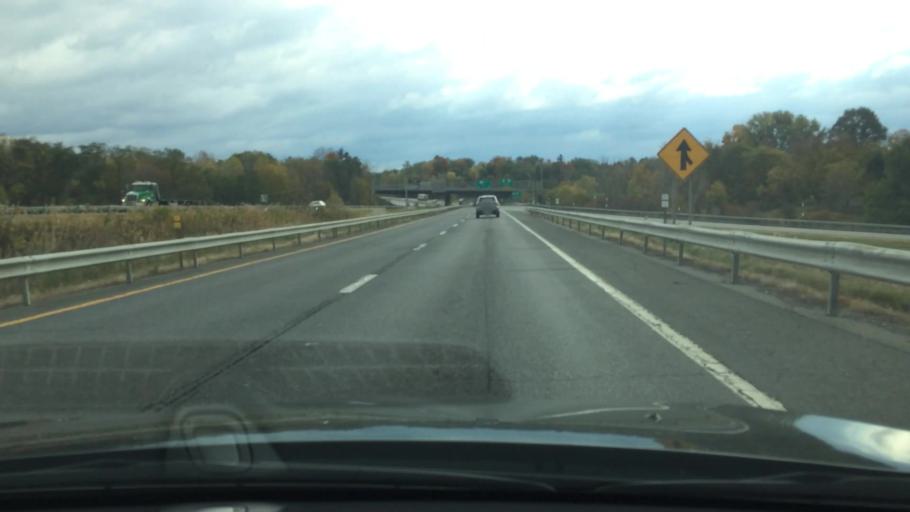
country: US
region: New York
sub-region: Albany County
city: Cohoes
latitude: 42.7623
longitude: -73.7613
